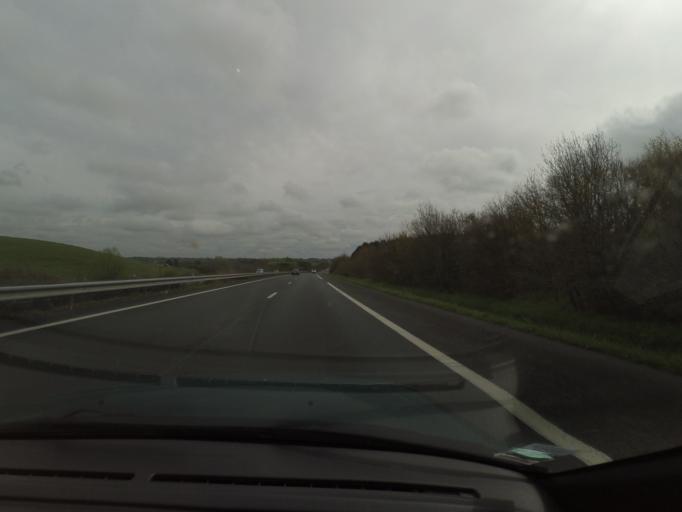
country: FR
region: Pays de la Loire
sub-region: Departement de Maine-et-Loire
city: Champtoce-sur-Loire
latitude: 47.4336
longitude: -0.8696
